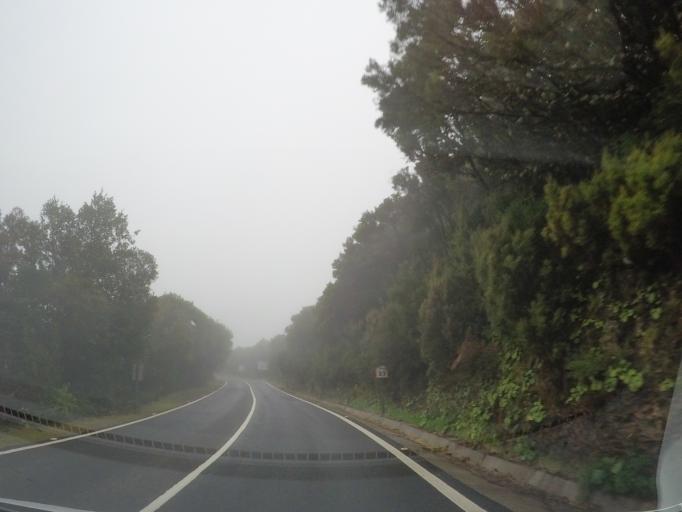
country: ES
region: Canary Islands
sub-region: Provincia de Santa Cruz de Tenerife
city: Alajero
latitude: 28.1092
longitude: -17.2429
